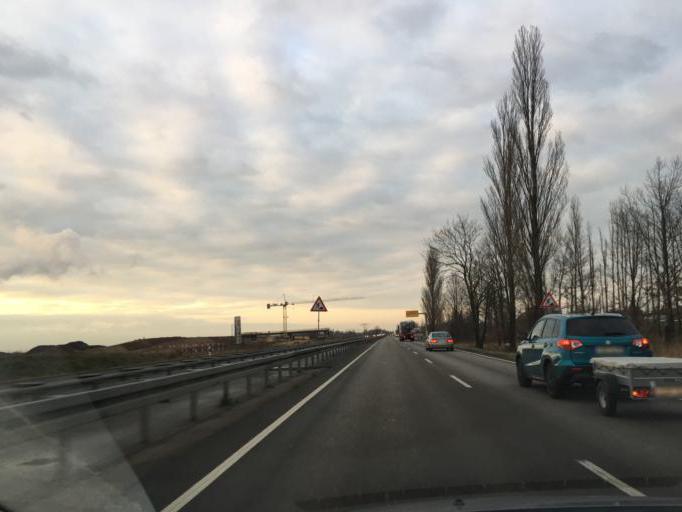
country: DE
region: Saxony
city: Espenhain
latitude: 51.1695
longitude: 12.4940
